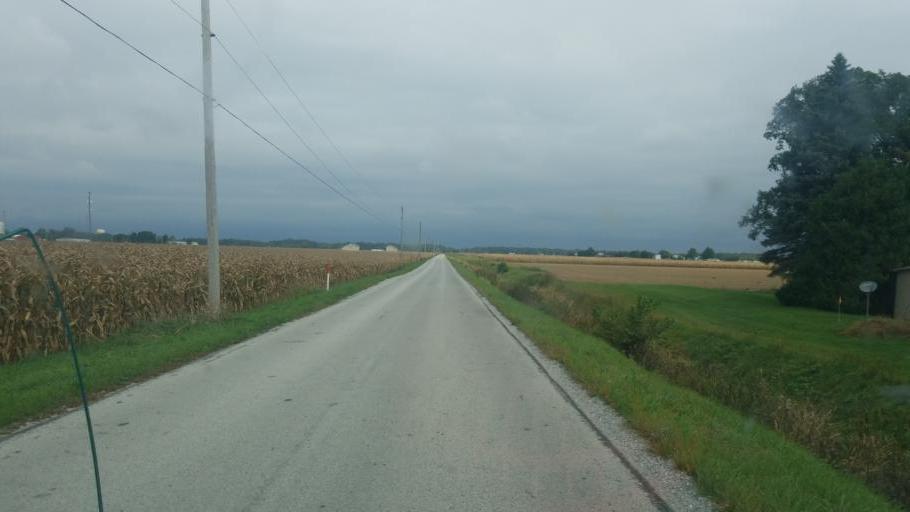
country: US
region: Ohio
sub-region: Wood County
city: Bowling Green
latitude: 41.3325
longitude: -83.6698
